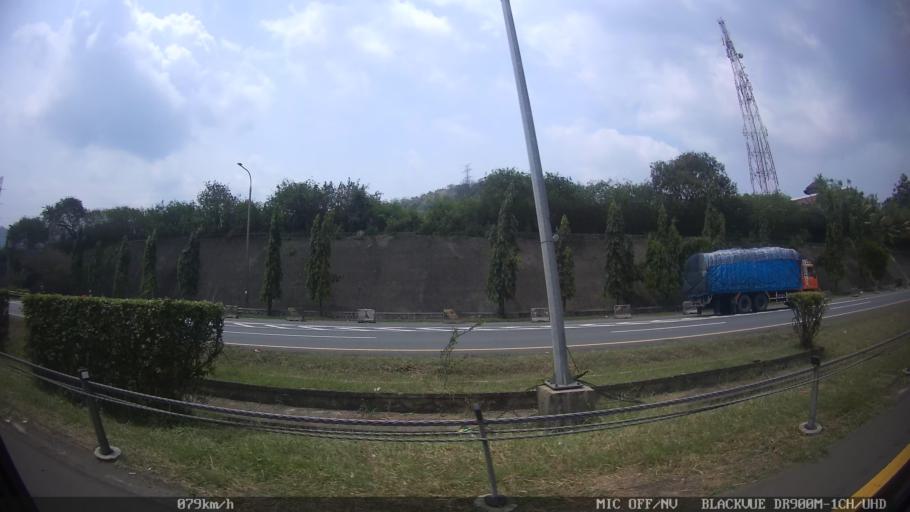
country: ID
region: Banten
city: Curug
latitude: -5.9851
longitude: 106.0347
